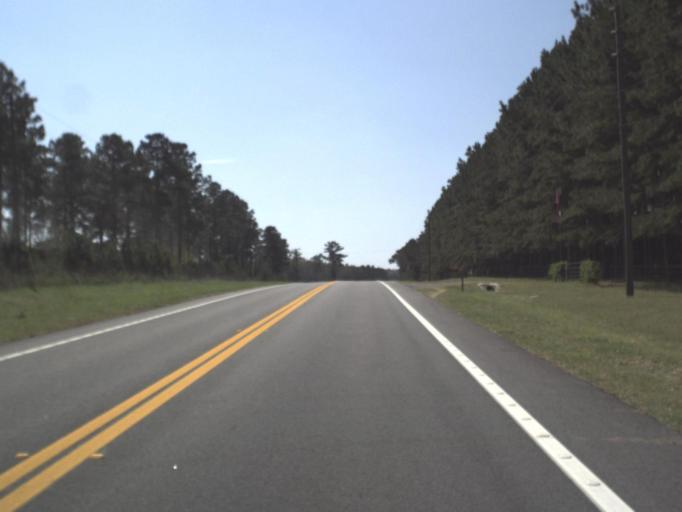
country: US
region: Florida
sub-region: Jefferson County
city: Monticello
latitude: 30.4556
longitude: -84.0189
